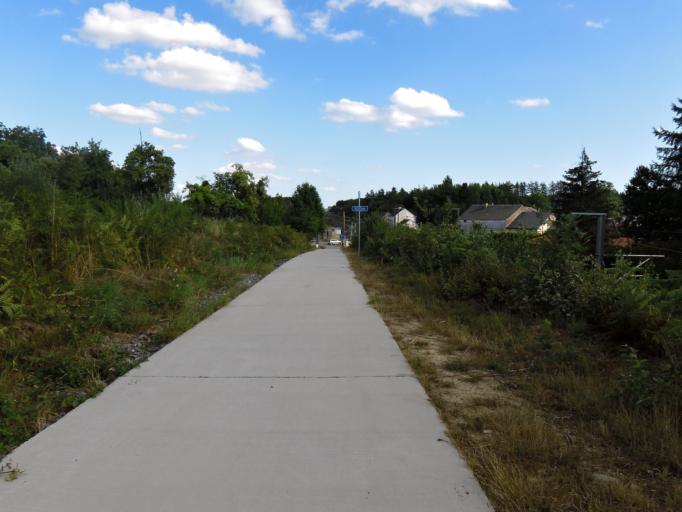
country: BE
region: Wallonia
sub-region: Province de Namur
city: Bievre
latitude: 49.9349
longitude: 5.0418
